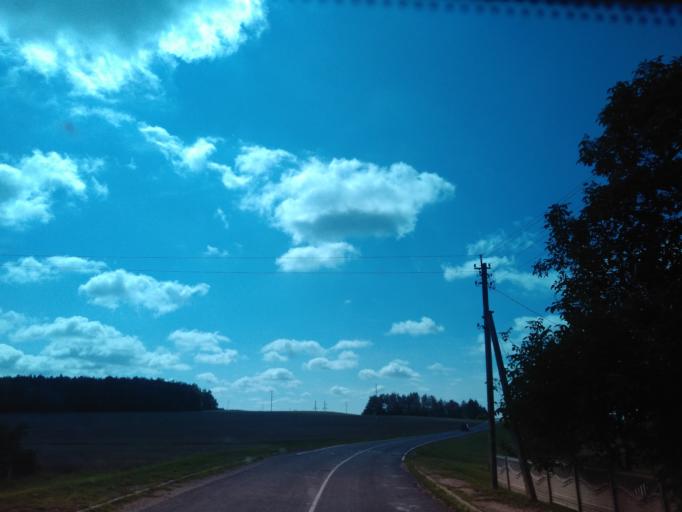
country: BY
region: Minsk
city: Uzda
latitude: 53.3863
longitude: 27.2429
